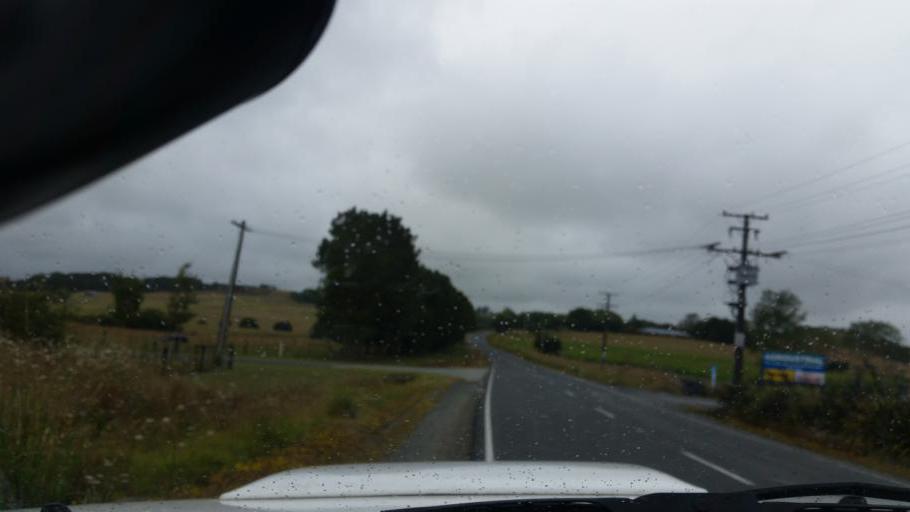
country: NZ
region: Auckland
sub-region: Auckland
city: Wellsford
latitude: -36.1382
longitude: 174.5151
